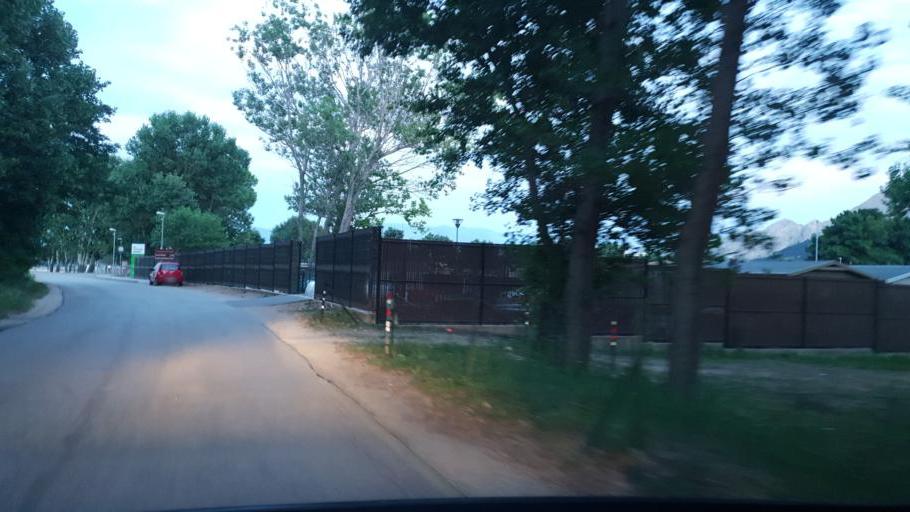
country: HR
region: Primorsko-Goranska
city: Punat
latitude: 44.9674
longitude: 14.7442
